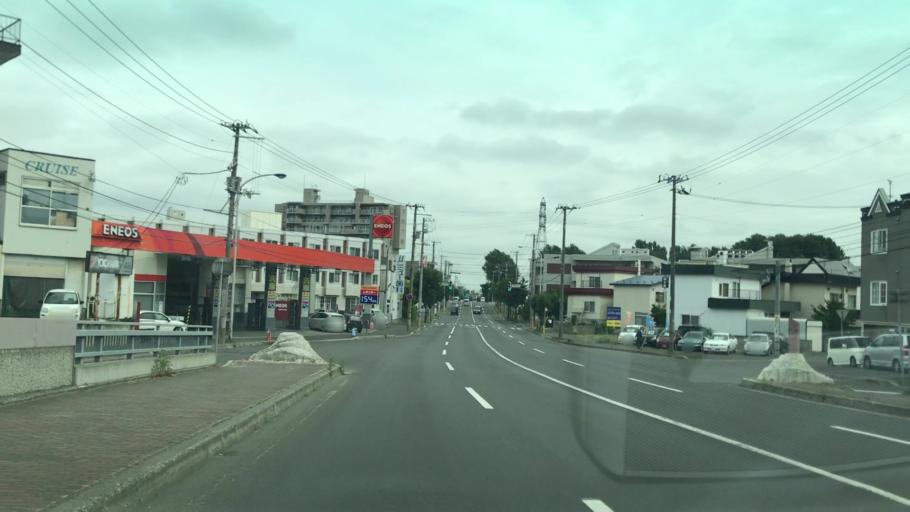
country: JP
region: Hokkaido
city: Sapporo
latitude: 43.0899
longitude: 141.2982
